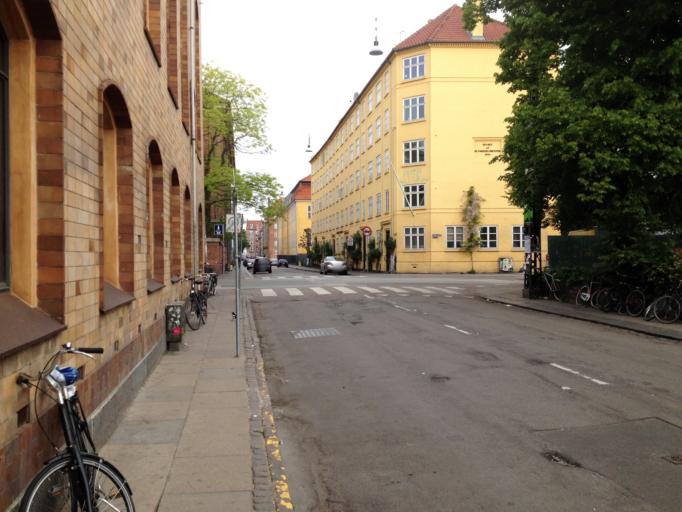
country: DK
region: Capital Region
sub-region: Kobenhavn
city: Christianshavn
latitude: 55.6731
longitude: 12.5964
